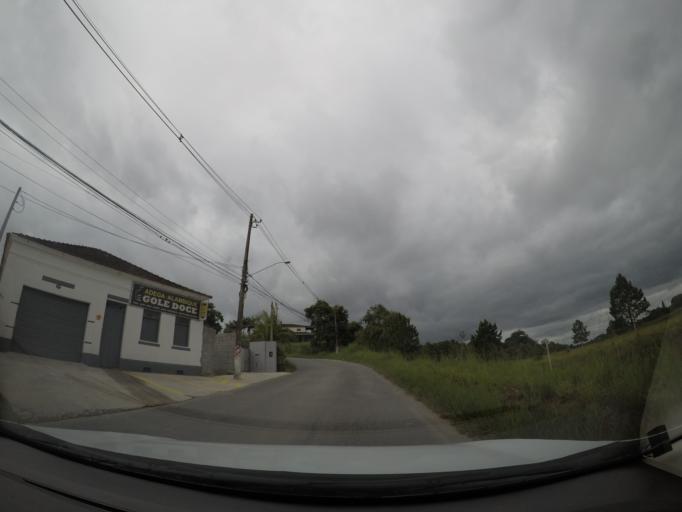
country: BR
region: Sao Paulo
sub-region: Aruja
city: Aruja
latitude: -23.3838
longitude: -46.3073
